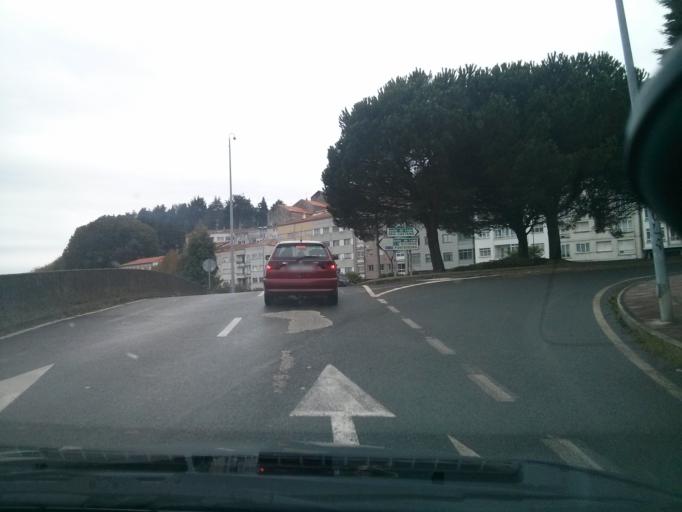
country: ES
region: Galicia
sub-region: Provincia da Coruna
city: Santiago de Compostela
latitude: 42.8785
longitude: -8.5329
